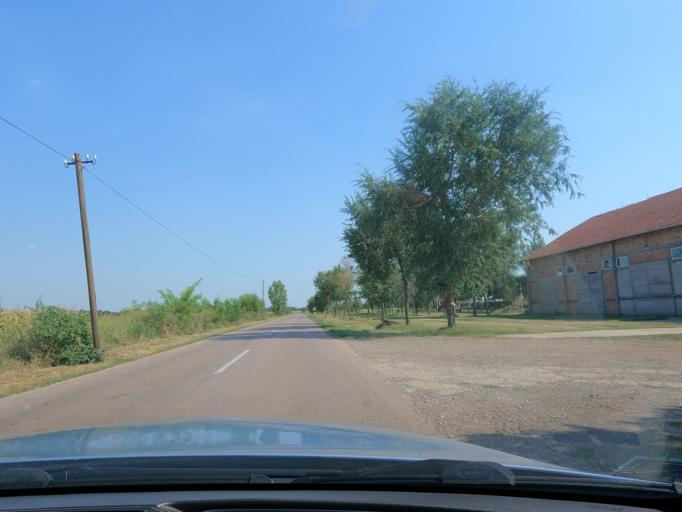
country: RS
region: Autonomna Pokrajina Vojvodina
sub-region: Severnobacki Okrug
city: Mali Igos
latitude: 45.7677
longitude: 19.7387
